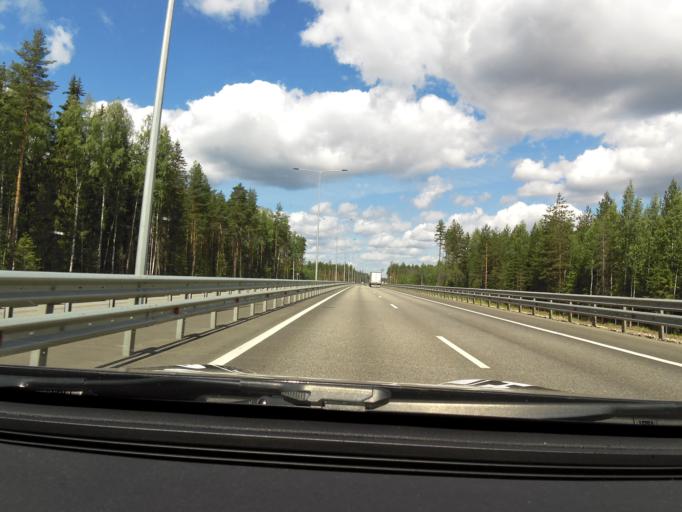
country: RU
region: Tverskaya
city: Krasnomayskiy
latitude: 57.5031
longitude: 34.2942
